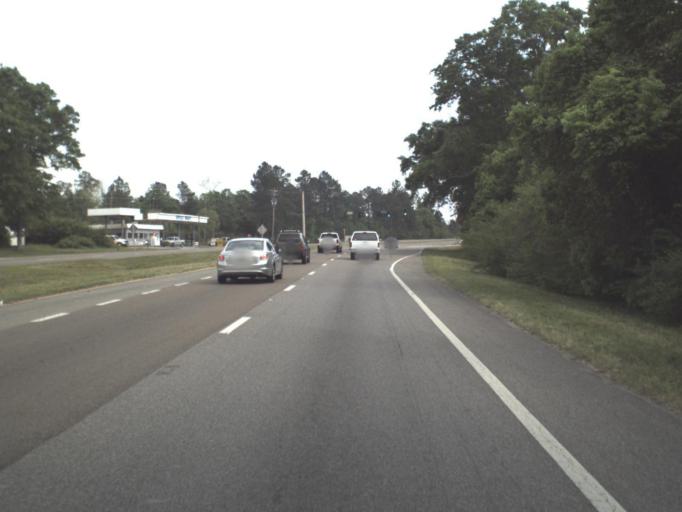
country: US
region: Florida
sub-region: Escambia County
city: Gonzalez
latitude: 30.5776
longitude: -87.2947
